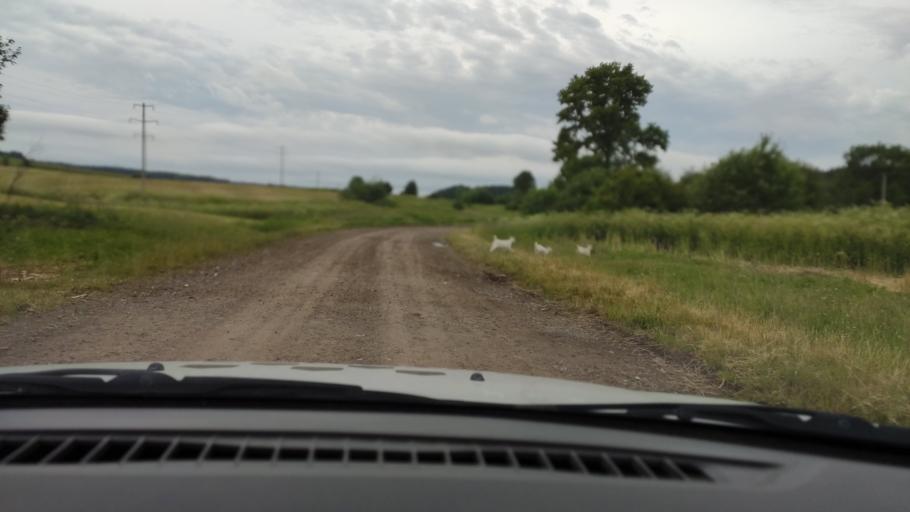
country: RU
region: Perm
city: Orda
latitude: 57.3014
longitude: 56.6179
